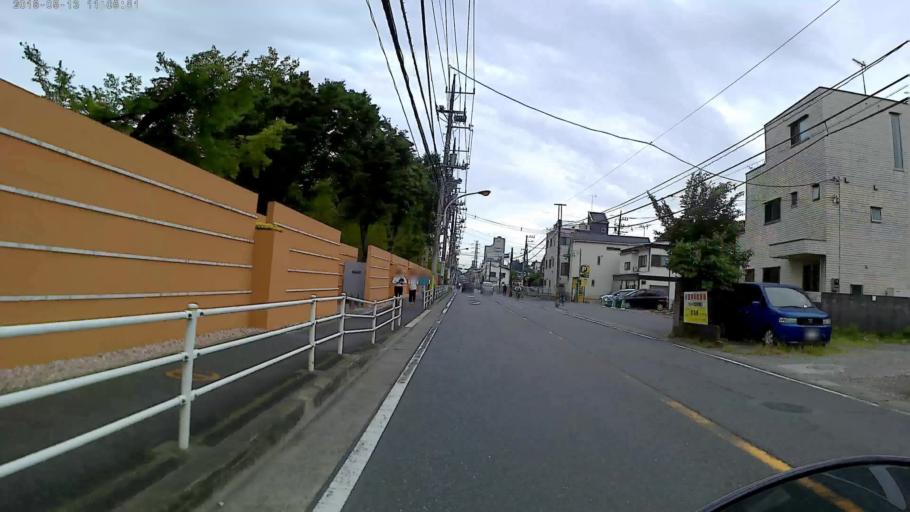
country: JP
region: Tokyo
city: Chofugaoka
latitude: 35.5937
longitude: 139.6145
